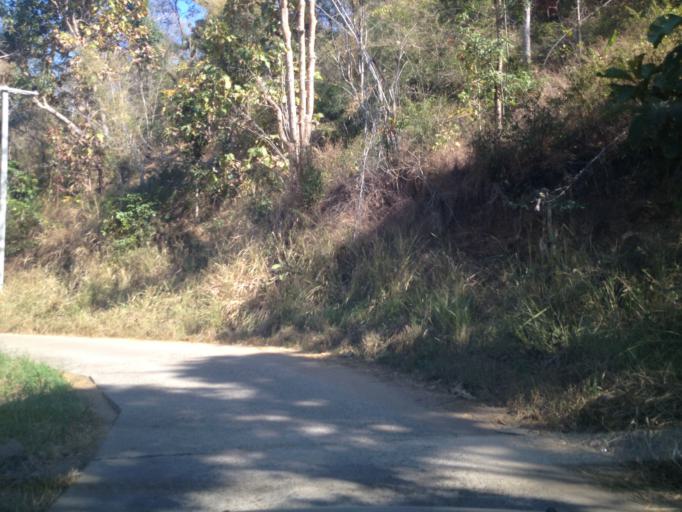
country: TH
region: Mae Hong Son
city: Ban Huai I Huak
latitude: 18.0685
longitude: 98.1837
